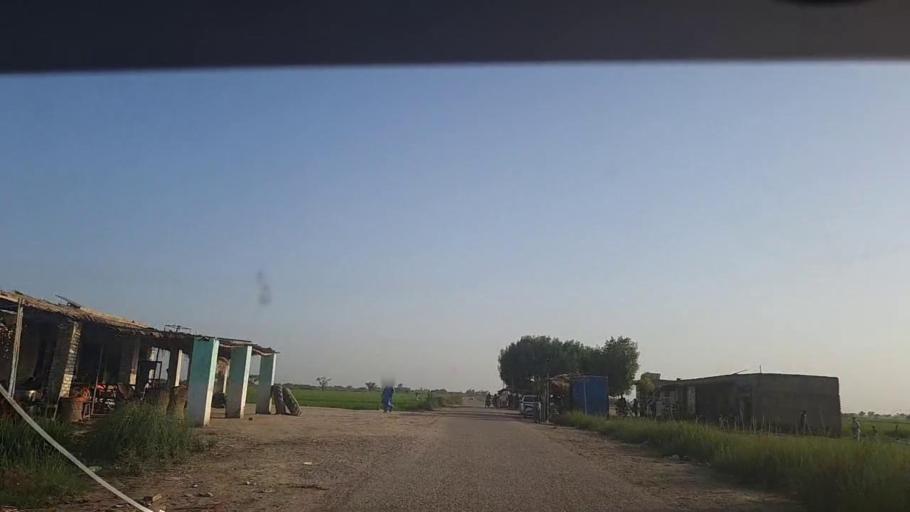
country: PK
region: Sindh
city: Thul
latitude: 28.1962
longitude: 68.8735
